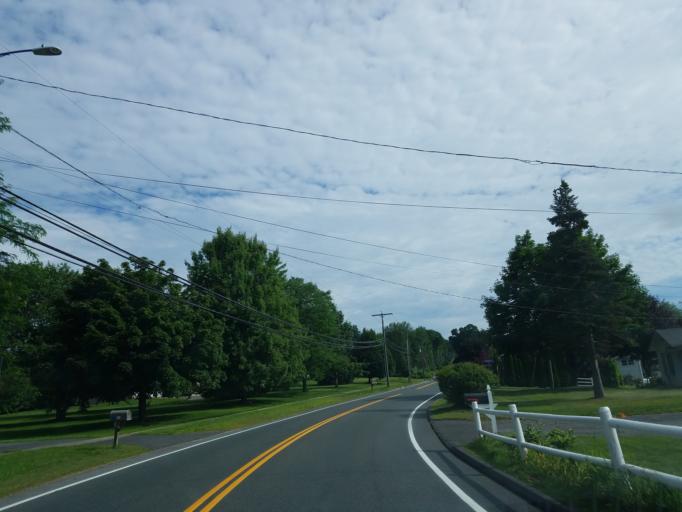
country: US
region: Connecticut
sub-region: Litchfield County
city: Plymouth
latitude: 41.6520
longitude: -73.0521
